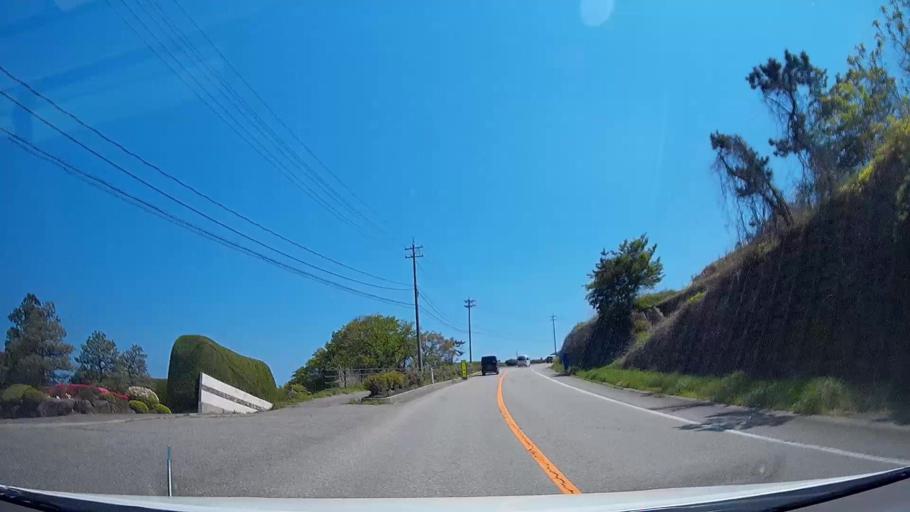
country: JP
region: Ishikawa
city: Nanao
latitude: 37.4019
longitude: 136.9474
